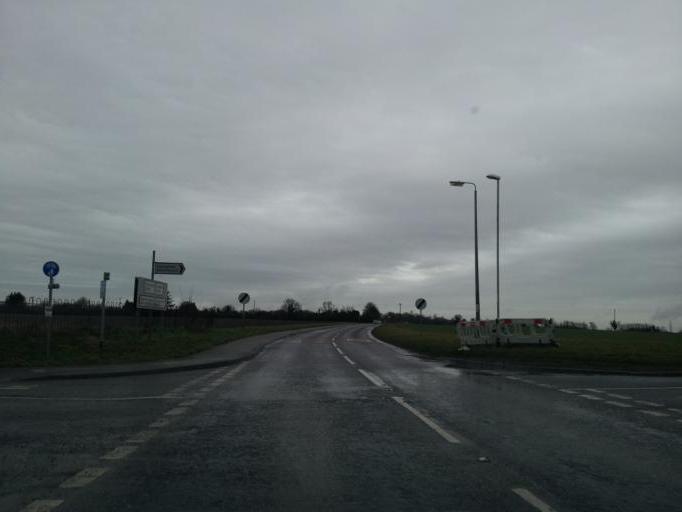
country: GB
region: England
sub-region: Cambridgeshire
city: Bottisham
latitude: 52.2419
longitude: 0.2820
